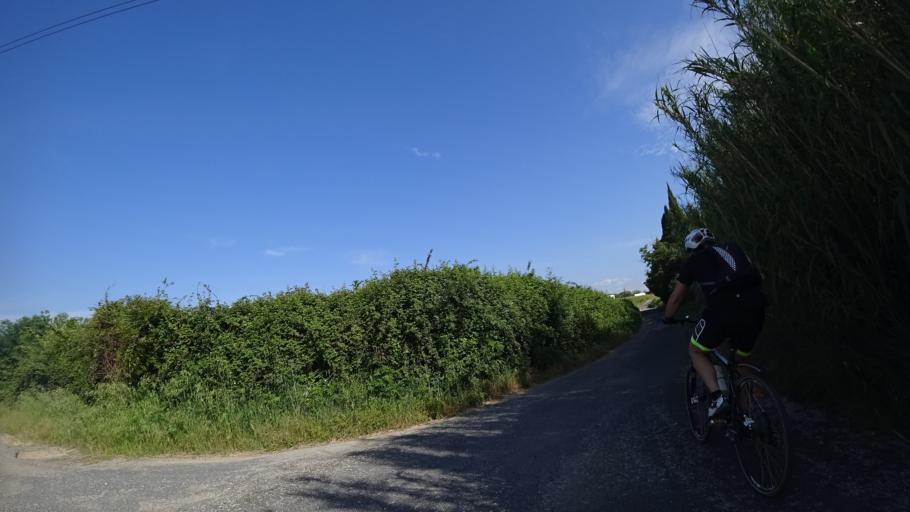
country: FR
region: Languedoc-Roussillon
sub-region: Departement de l'Herault
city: Olonzac
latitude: 43.2618
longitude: 2.7216
